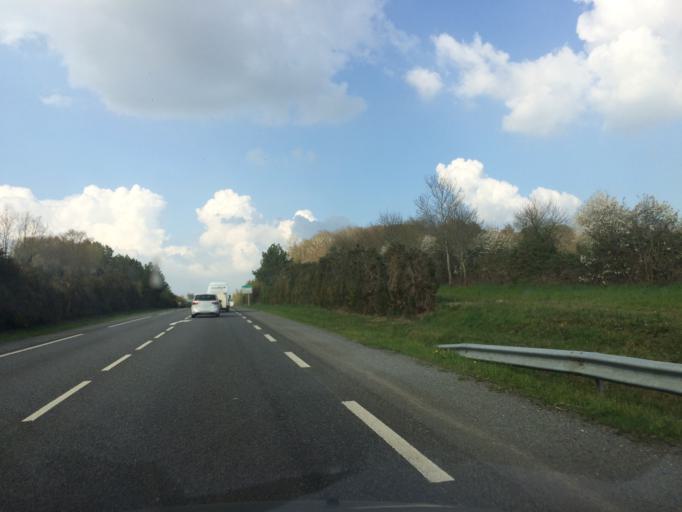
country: FR
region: Pays de la Loire
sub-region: Departement de la Loire-Atlantique
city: Saint-Nicolas-de-Redon
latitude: 47.6404
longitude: -2.0512
